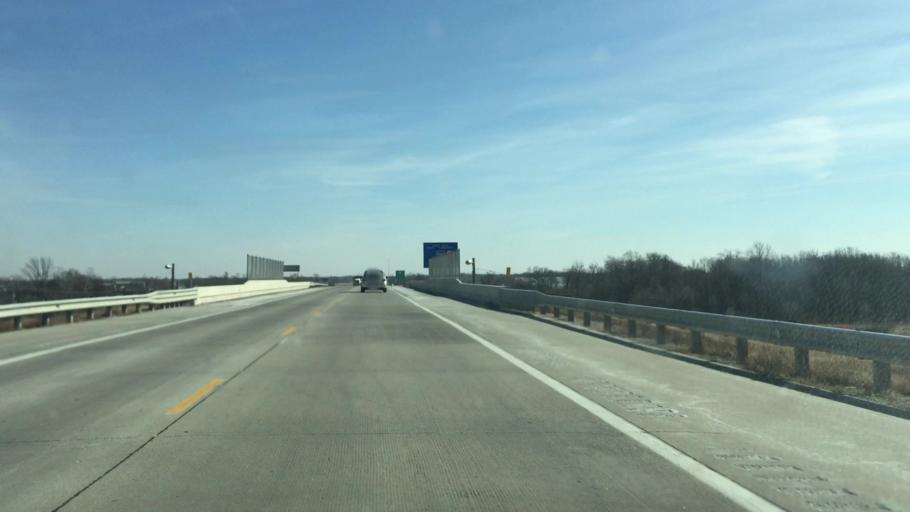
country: US
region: Kansas
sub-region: Labette County
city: Parsons
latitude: 37.3693
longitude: -95.2755
